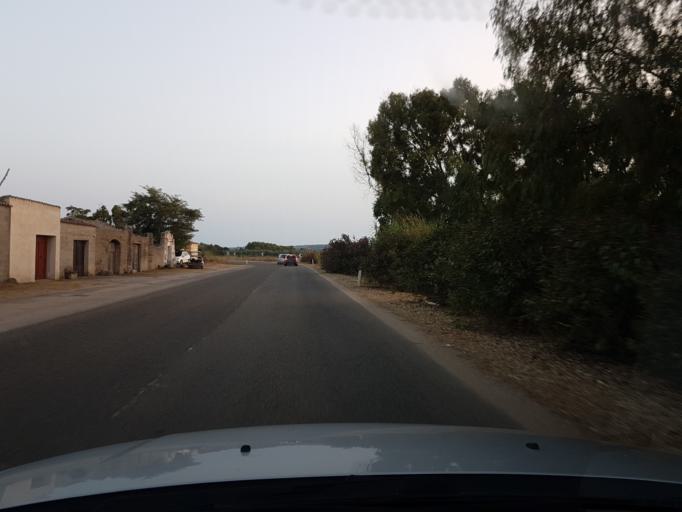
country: IT
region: Sardinia
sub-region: Provincia di Oristano
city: Cabras
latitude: 39.9216
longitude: 8.4514
